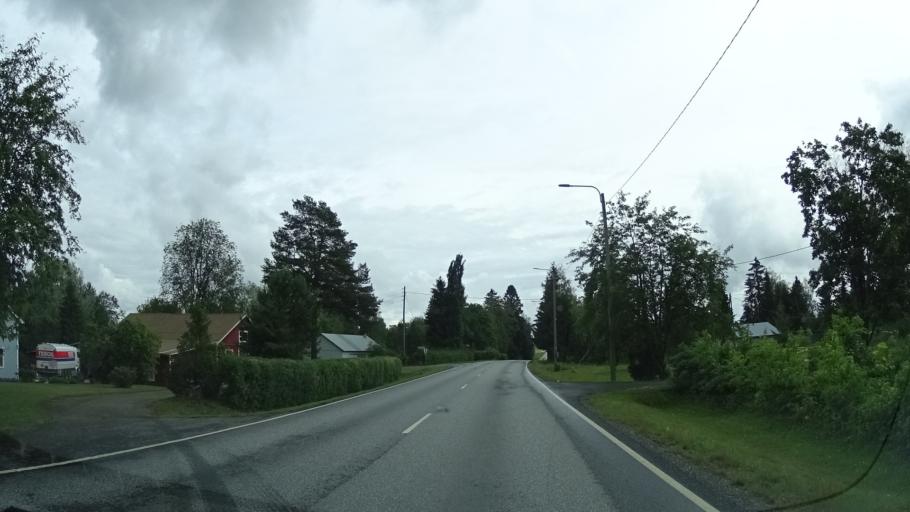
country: FI
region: Pirkanmaa
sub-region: Lounais-Pirkanmaa
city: Punkalaidun
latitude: 61.1016
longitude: 23.2860
